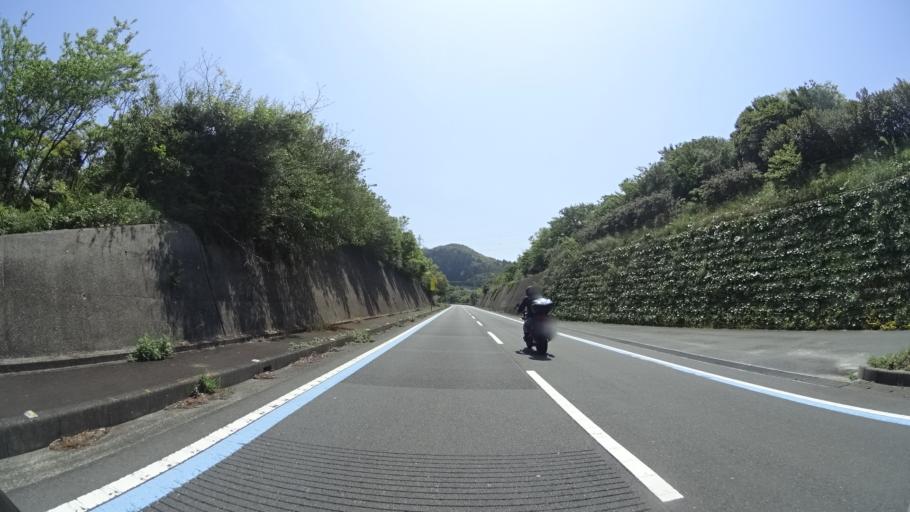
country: JP
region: Ehime
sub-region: Nishiuwa-gun
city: Ikata-cho
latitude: 33.4475
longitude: 132.2593
